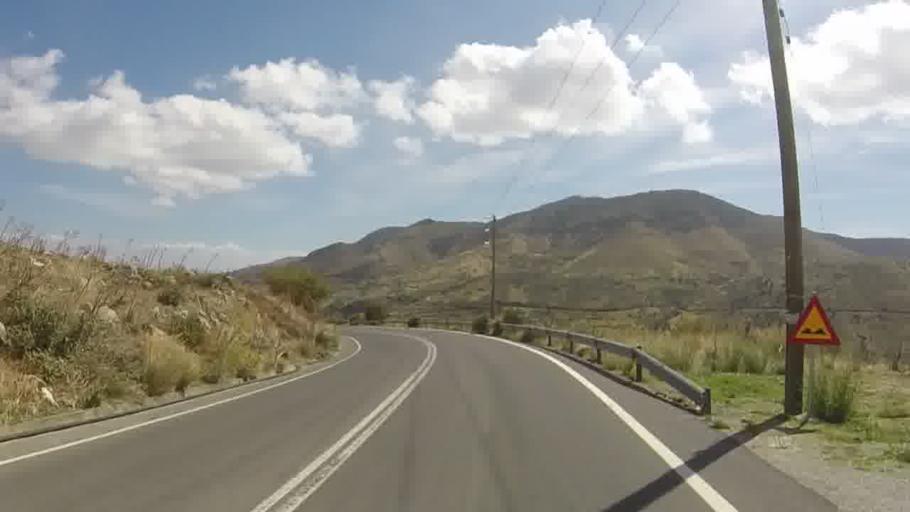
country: GR
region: Crete
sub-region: Nomos Rethymnis
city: Agia Galini
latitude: 35.1490
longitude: 24.6280
